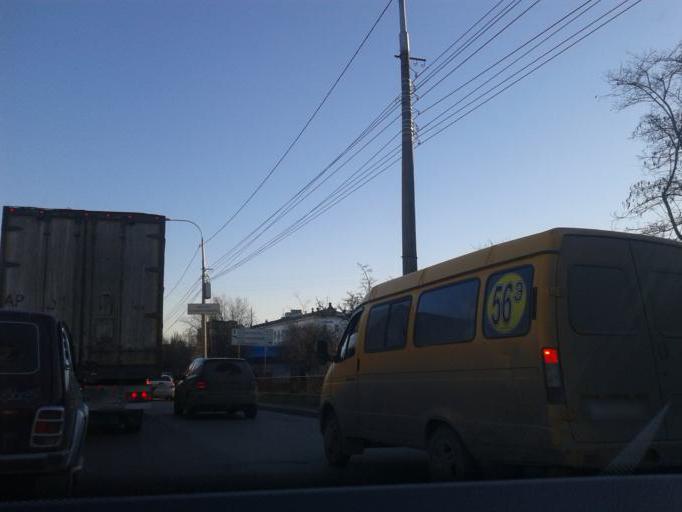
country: RU
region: Volgograd
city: Volgograd
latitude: 48.6603
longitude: 44.4385
